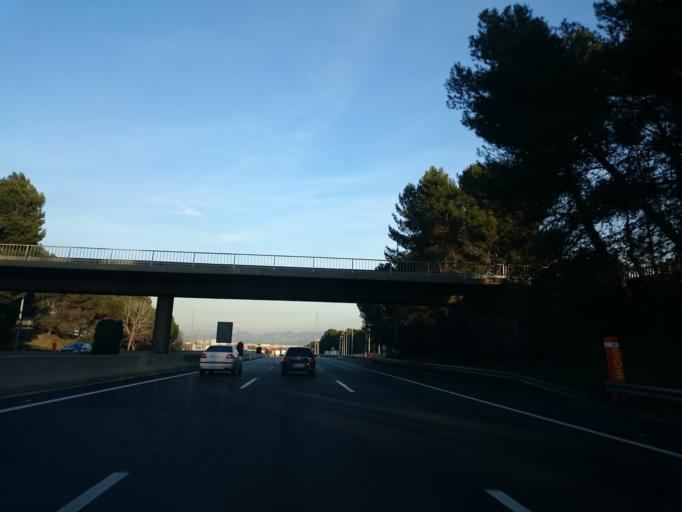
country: ES
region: Catalonia
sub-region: Provincia de Barcelona
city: Sant Cugat del Valles
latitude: 41.4926
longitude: 2.1000
